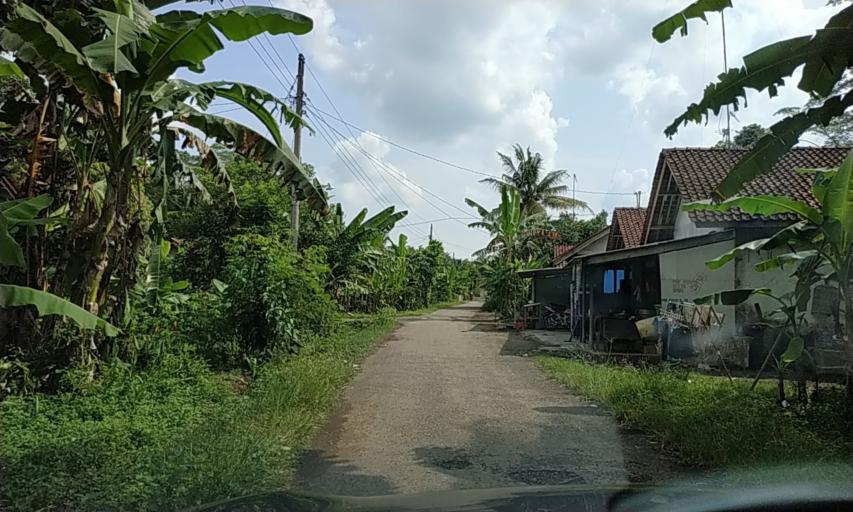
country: ID
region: Central Java
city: Bakung
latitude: -7.3489
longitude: 108.6648
